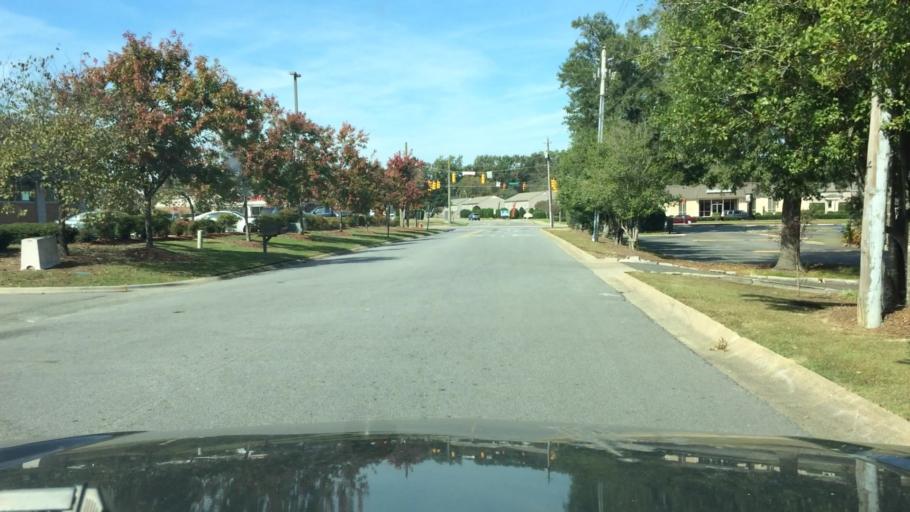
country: US
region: North Carolina
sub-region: Wayne County
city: Goldsboro
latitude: 35.3972
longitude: -77.9617
